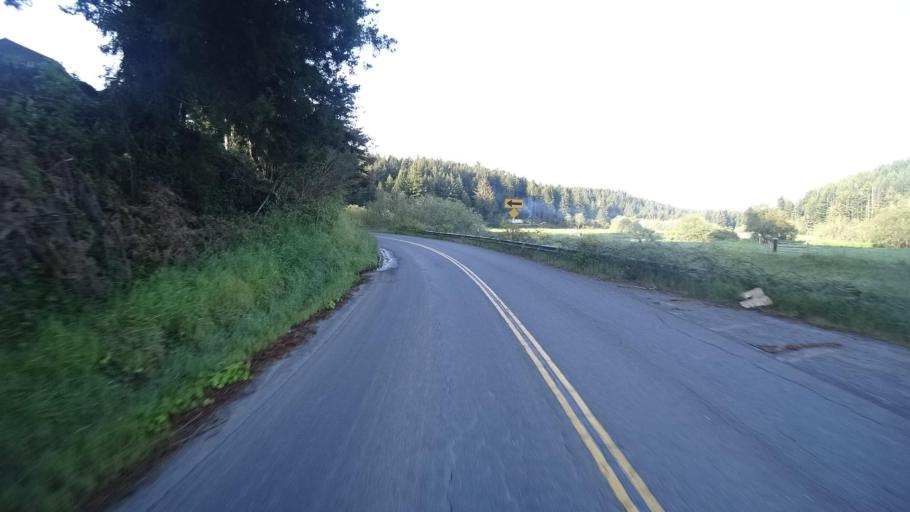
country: US
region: California
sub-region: Humboldt County
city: Myrtletown
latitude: 40.7785
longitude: -124.1185
